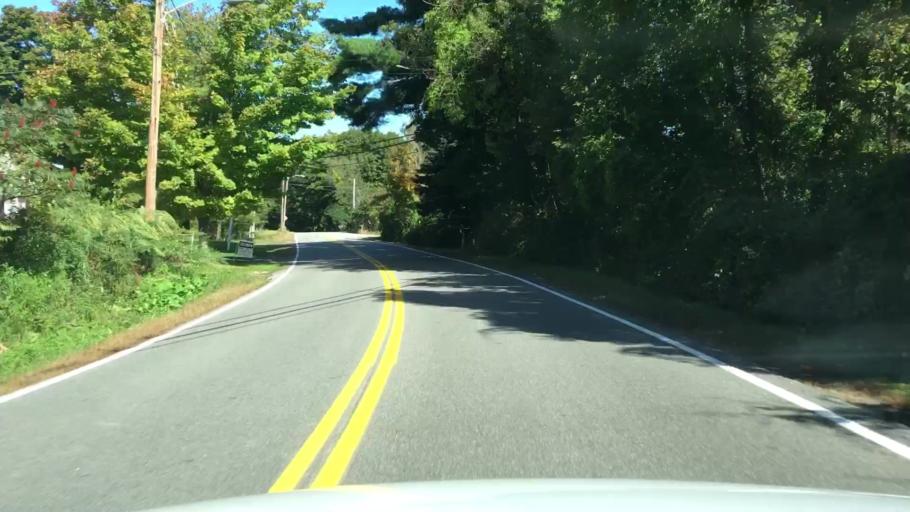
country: US
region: Maine
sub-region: York County
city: Kittery Point
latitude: 43.0999
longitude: -70.6751
